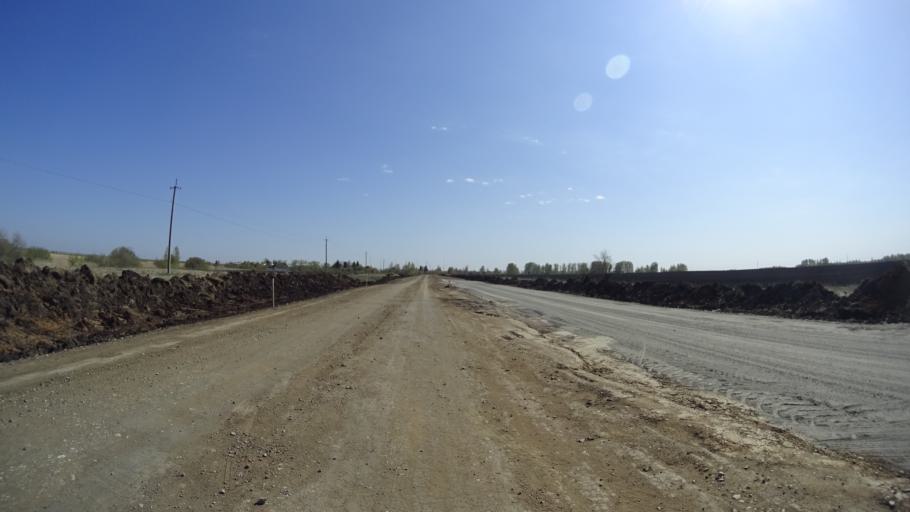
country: RU
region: Chelyabinsk
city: Troitsk
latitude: 54.1845
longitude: 61.4935
